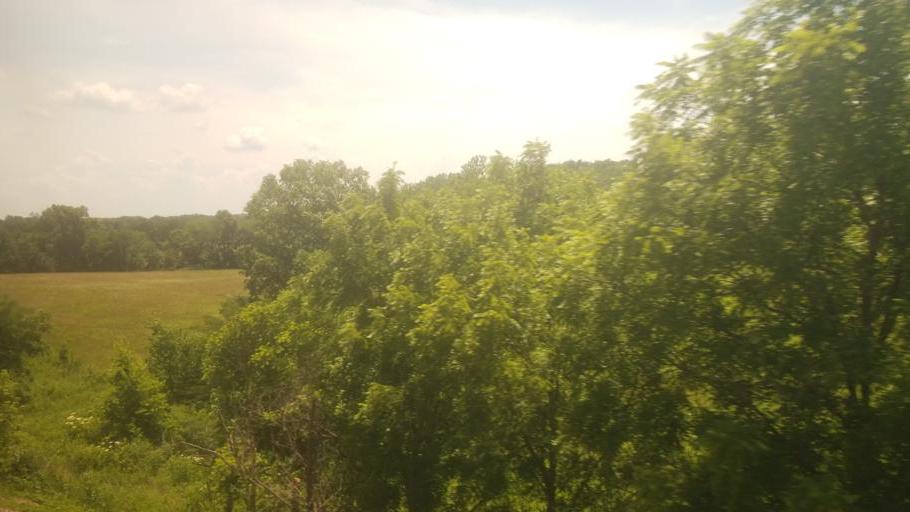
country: US
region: Missouri
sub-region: Linn County
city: Marceline
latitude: 39.8669
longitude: -92.7944
